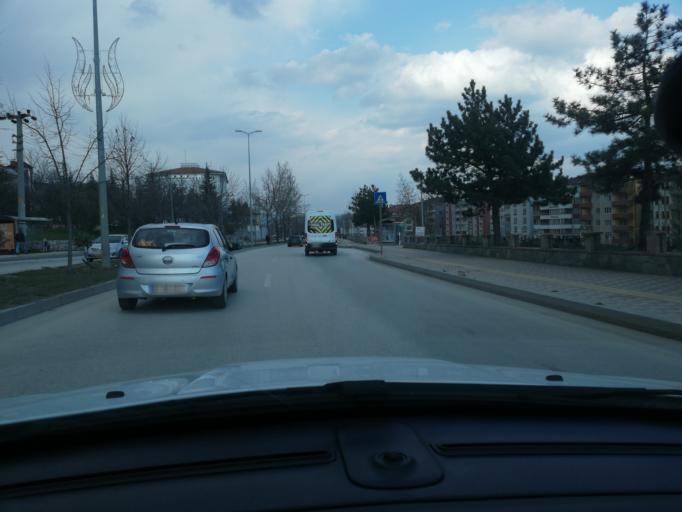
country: TR
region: Kastamonu
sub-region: Cide
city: Kastamonu
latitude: 41.4008
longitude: 33.7813
